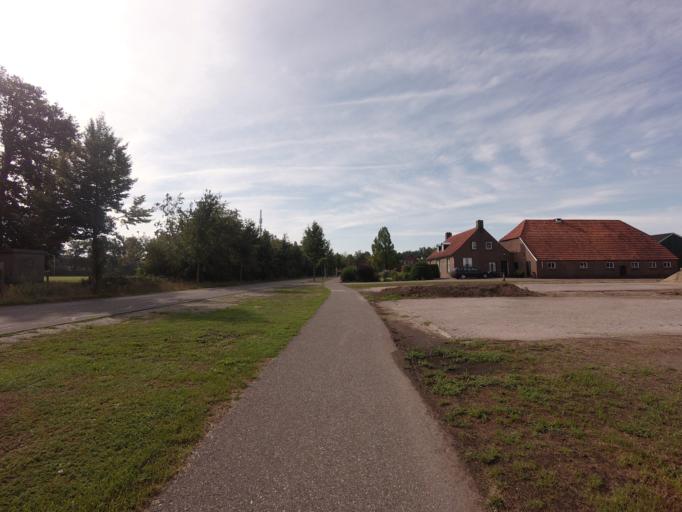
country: NL
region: Gelderland
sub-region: Gemeente Lochem
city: Harfsen
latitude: 52.2806
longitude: 6.2726
